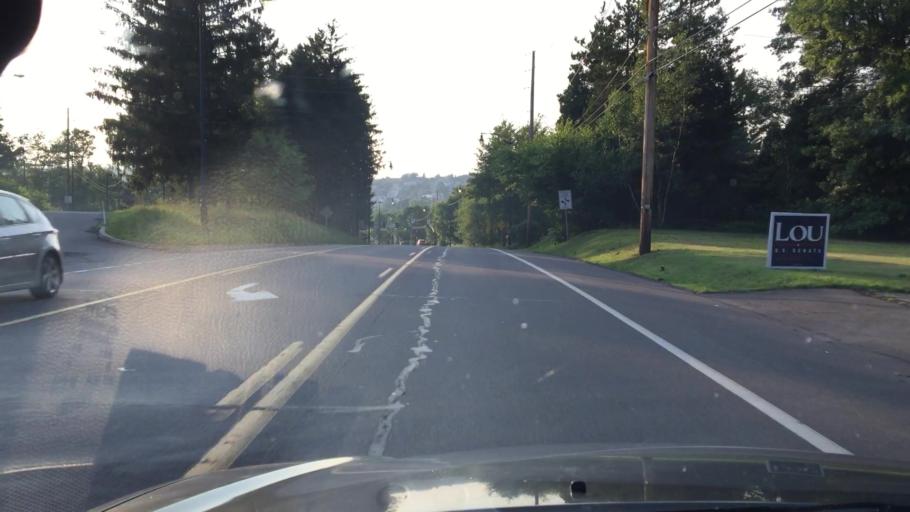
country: US
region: Pennsylvania
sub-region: Luzerne County
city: Hazleton
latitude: 40.9485
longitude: -75.9609
